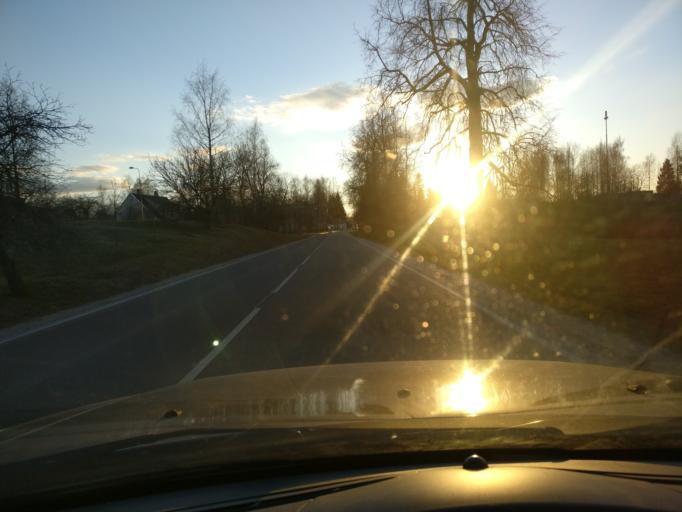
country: LV
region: Aluksnes Rajons
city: Aluksne
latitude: 57.4192
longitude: 27.0718
